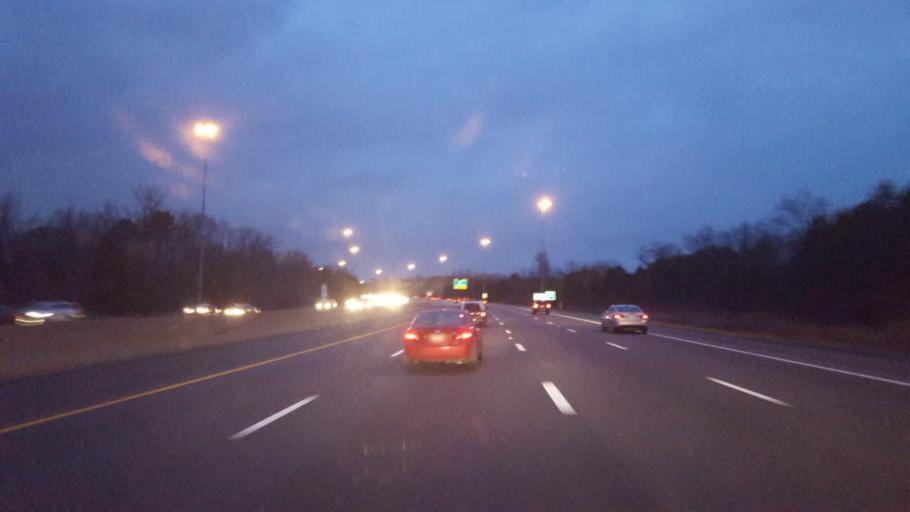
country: US
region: Ohio
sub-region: Franklin County
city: Reynoldsburg
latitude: 39.9647
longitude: -82.8429
